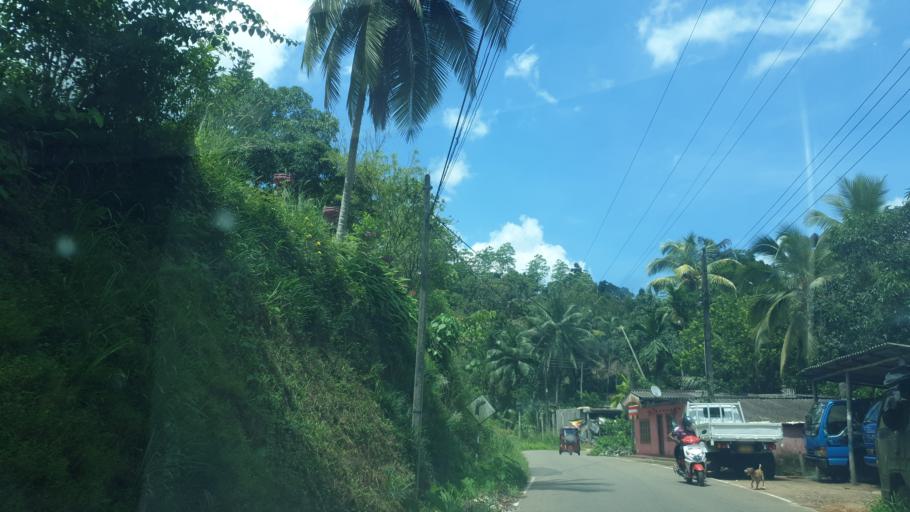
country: LK
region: Sabaragamuwa
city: Ratnapura
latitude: 6.4664
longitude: 80.4292
